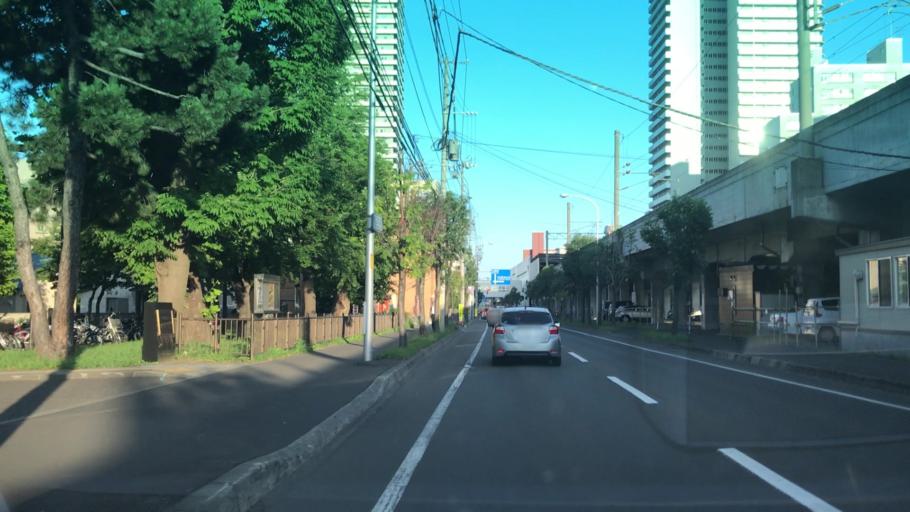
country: JP
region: Hokkaido
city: Sapporo
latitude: 43.0833
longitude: 141.3047
